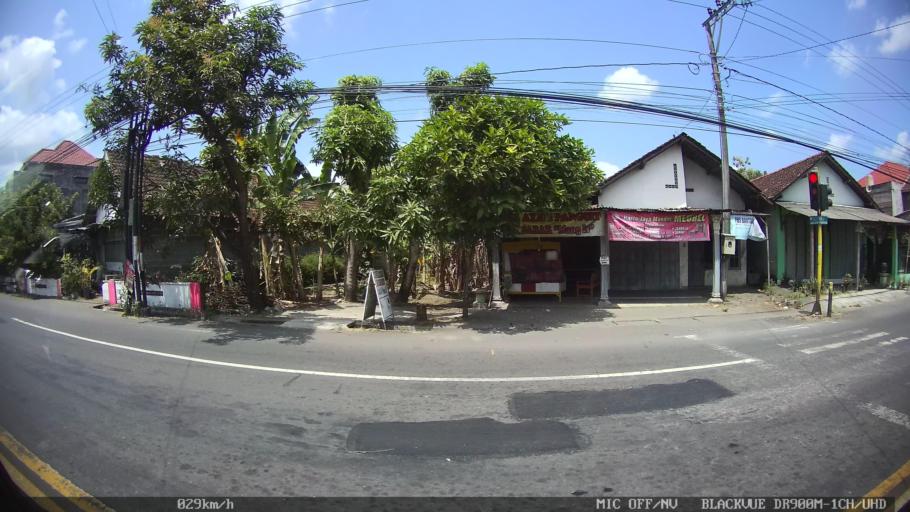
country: ID
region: Daerah Istimewa Yogyakarta
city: Pandak
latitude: -7.9065
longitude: 110.3109
